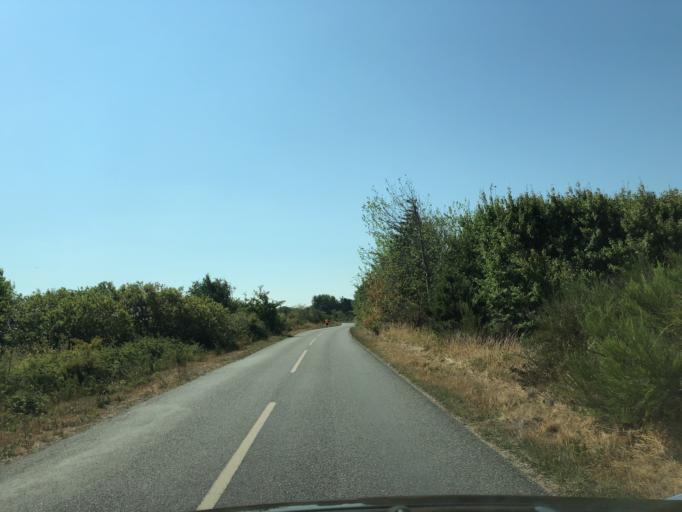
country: DK
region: Zealand
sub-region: Odsherred Kommune
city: Asnaes
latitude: 55.9966
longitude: 11.2895
